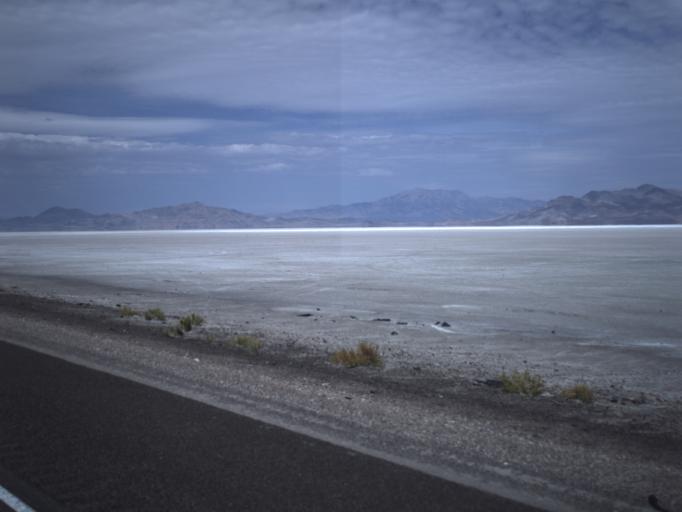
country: US
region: Utah
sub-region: Tooele County
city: Wendover
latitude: 40.7360
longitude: -113.6848
